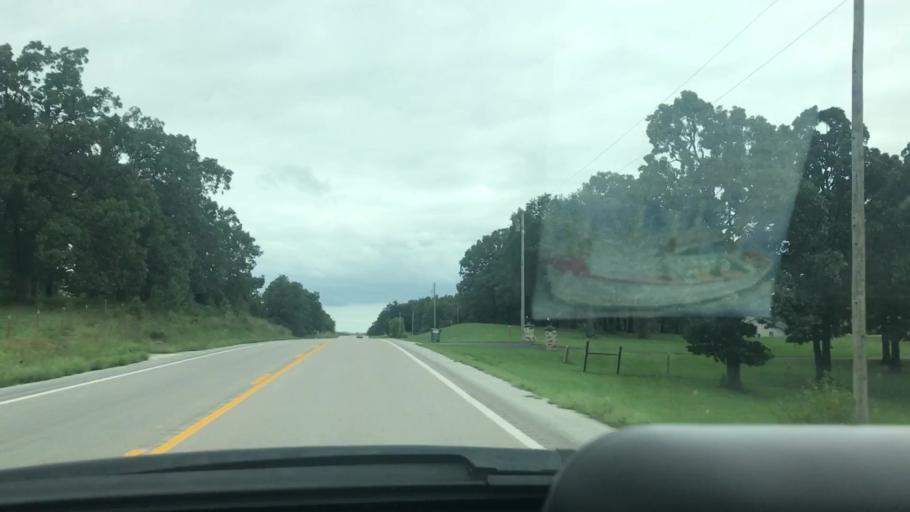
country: US
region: Missouri
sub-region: Dallas County
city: Buffalo
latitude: 37.7101
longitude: -93.1143
